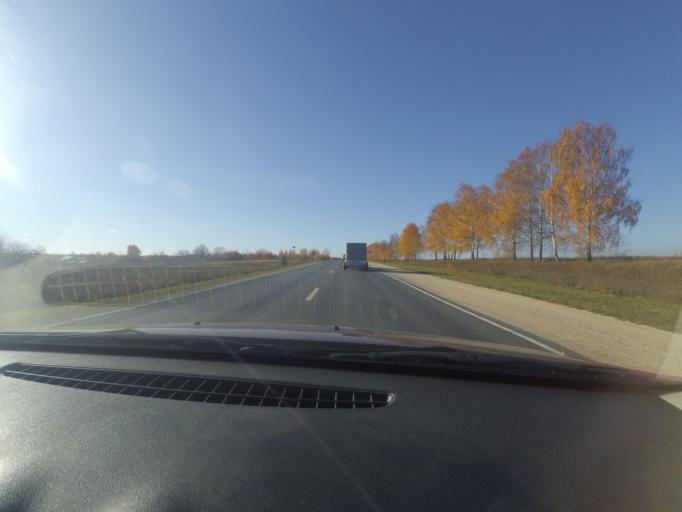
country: RU
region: Nizjnij Novgorod
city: Taremskoye
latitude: 55.8809
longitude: 42.9094
